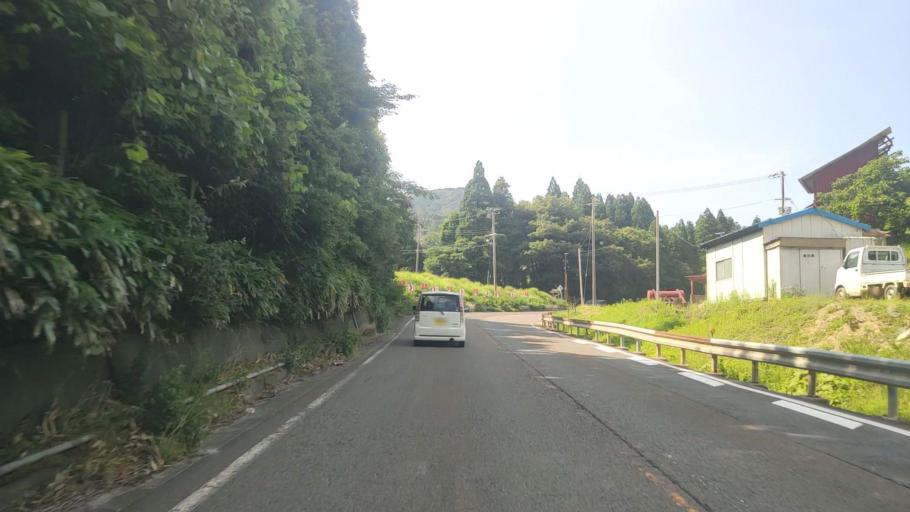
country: JP
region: Fukui
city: Tsuruga
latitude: 35.5732
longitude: 136.1230
